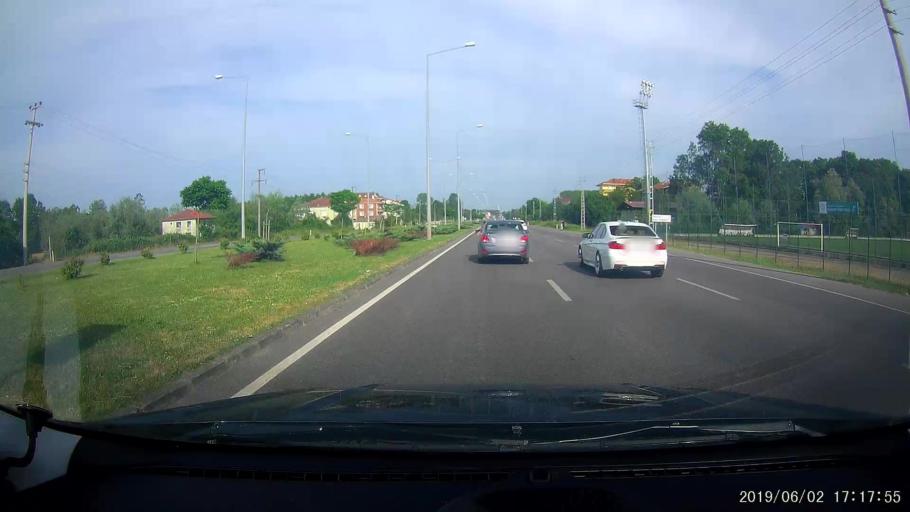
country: TR
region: Samsun
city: Dikbiyik
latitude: 41.2262
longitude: 36.5894
